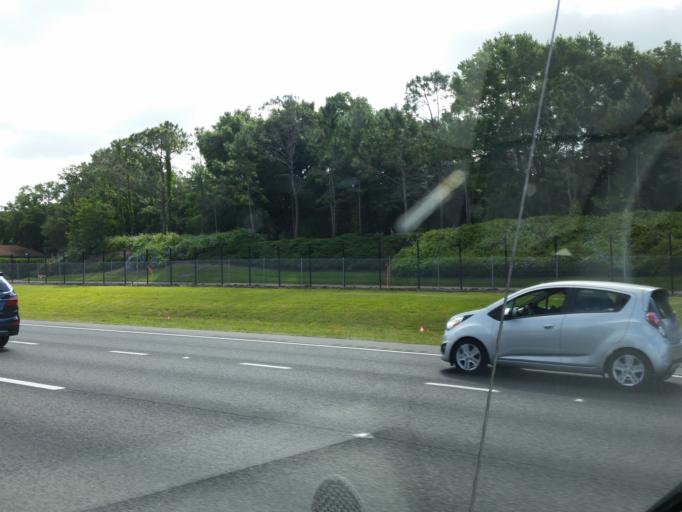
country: US
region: Florida
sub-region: Osceola County
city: Celebration
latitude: 28.3708
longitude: -81.5103
